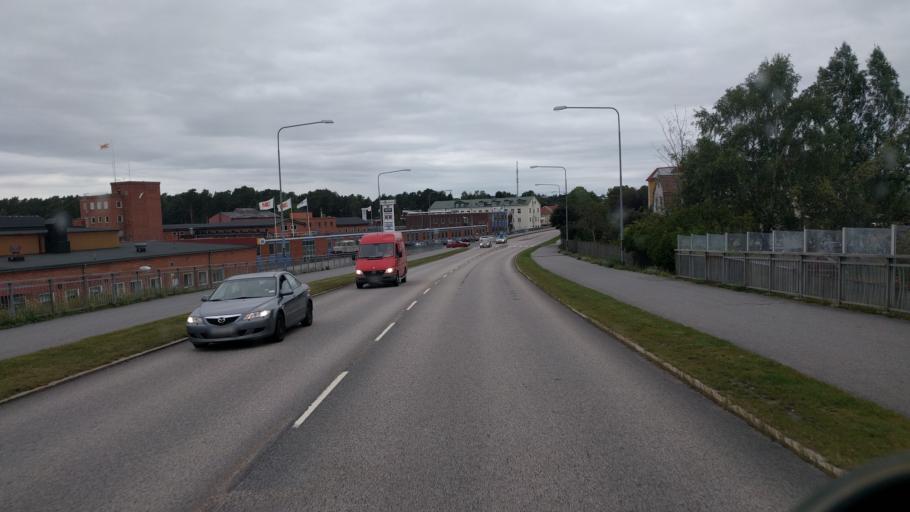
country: SE
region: Kalmar
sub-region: Vasterviks Kommun
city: Vaestervik
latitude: 57.7527
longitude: 16.6271
